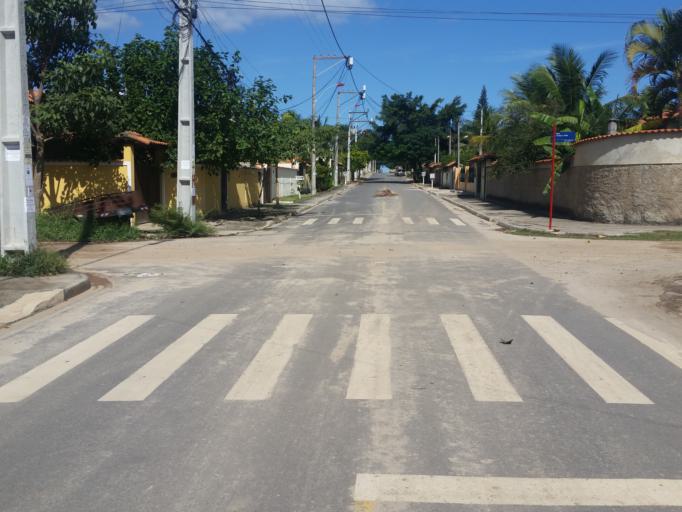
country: BR
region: Rio de Janeiro
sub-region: Marica
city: Marica
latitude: -22.9620
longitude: -42.9667
